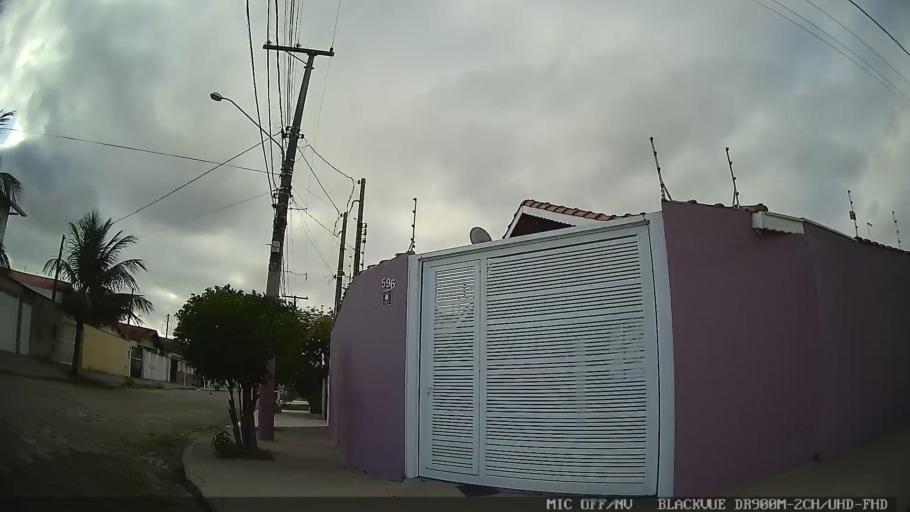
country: BR
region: Sao Paulo
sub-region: Peruibe
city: Peruibe
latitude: -24.3088
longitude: -46.9870
